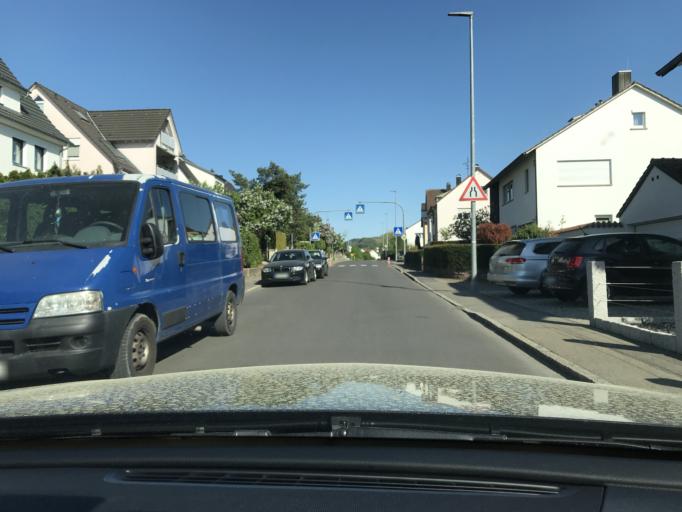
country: DE
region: Baden-Wuerttemberg
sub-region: Regierungsbezirk Stuttgart
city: Weinstadt-Endersbach
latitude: 48.8104
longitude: 9.3704
